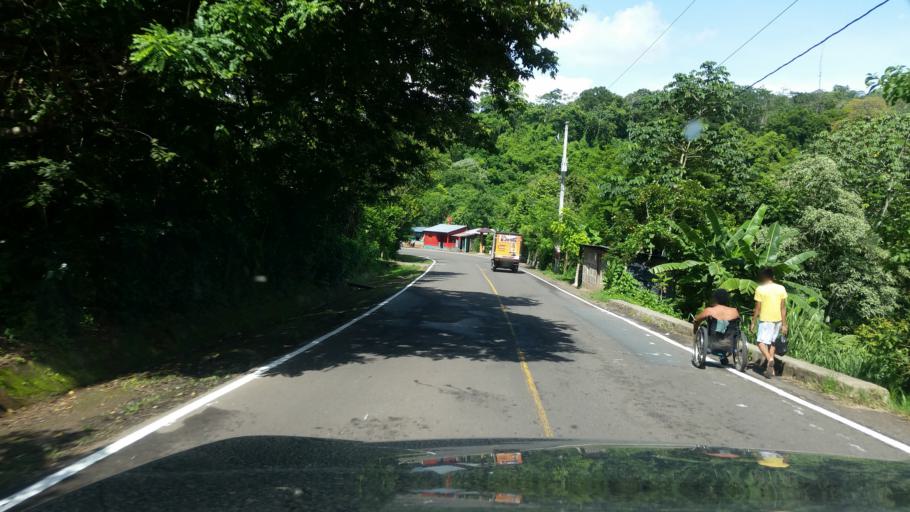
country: NI
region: Matagalpa
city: San Ramon
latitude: 12.9993
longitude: -85.8116
